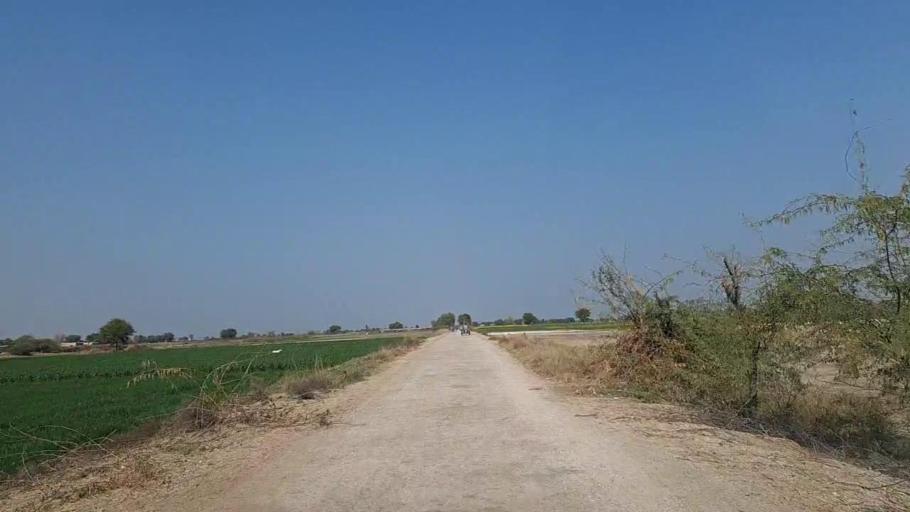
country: PK
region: Sindh
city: Nawabshah
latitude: 26.2673
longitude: 68.5133
